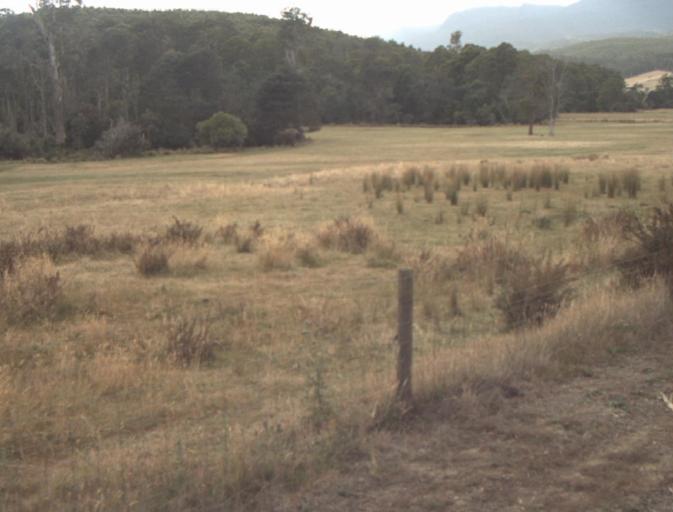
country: AU
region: Tasmania
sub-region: Northern Midlands
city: Evandale
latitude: -41.4597
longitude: 147.5327
